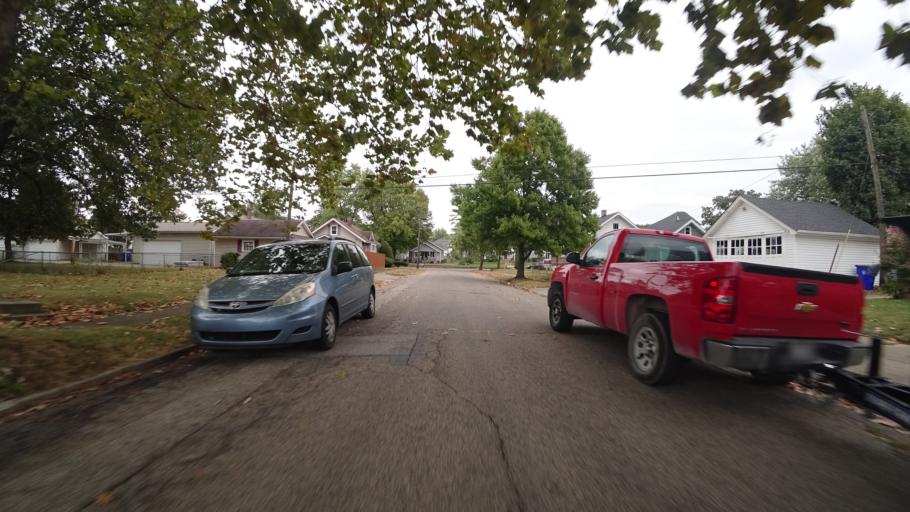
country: US
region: Ohio
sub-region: Butler County
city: Fairfield
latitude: 39.3651
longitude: -84.5602
